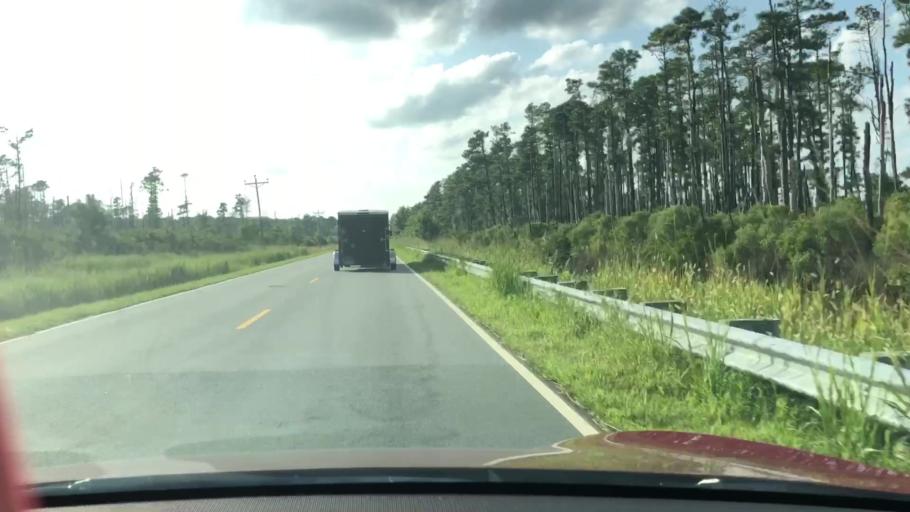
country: US
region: North Carolina
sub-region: Dare County
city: Wanchese
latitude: 35.6105
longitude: -75.8228
